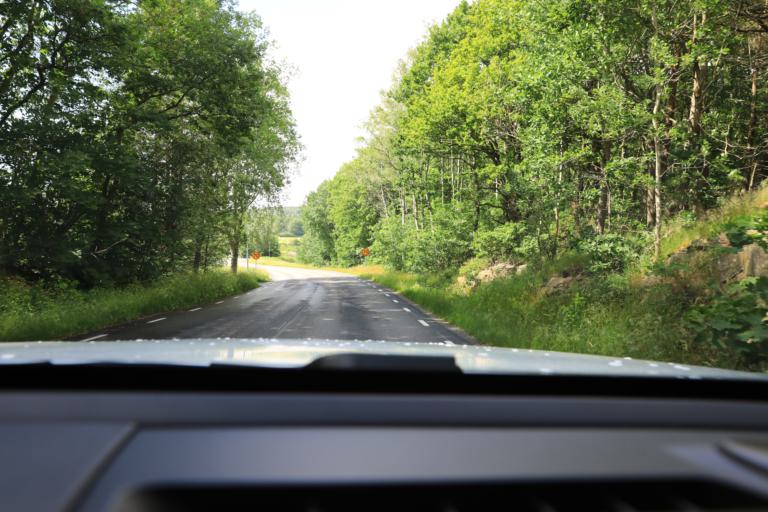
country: SE
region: Halland
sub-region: Varbergs Kommun
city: Varberg
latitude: 57.1743
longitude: 12.2887
